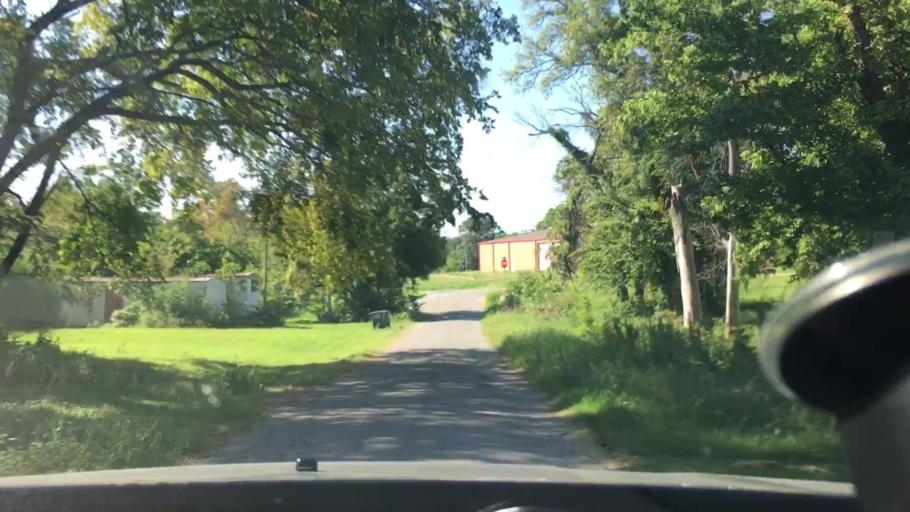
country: US
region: Oklahoma
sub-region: Johnston County
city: Tishomingo
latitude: 34.2411
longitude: -96.5474
